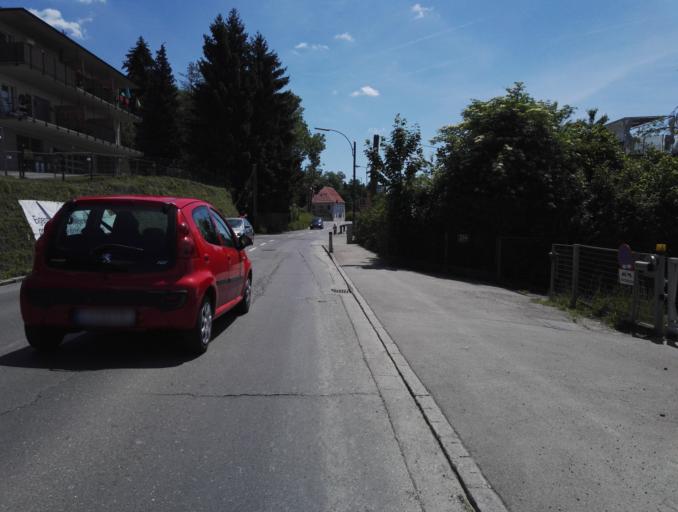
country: AT
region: Styria
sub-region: Politischer Bezirk Graz-Umgebung
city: Raaba
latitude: 47.0447
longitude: 15.4866
